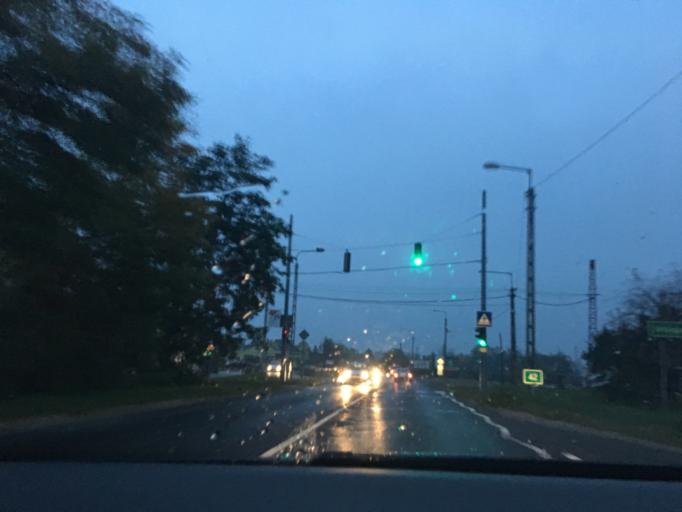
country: HU
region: Pest
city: Nyaregyhaza
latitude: 47.3088
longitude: 19.4998
